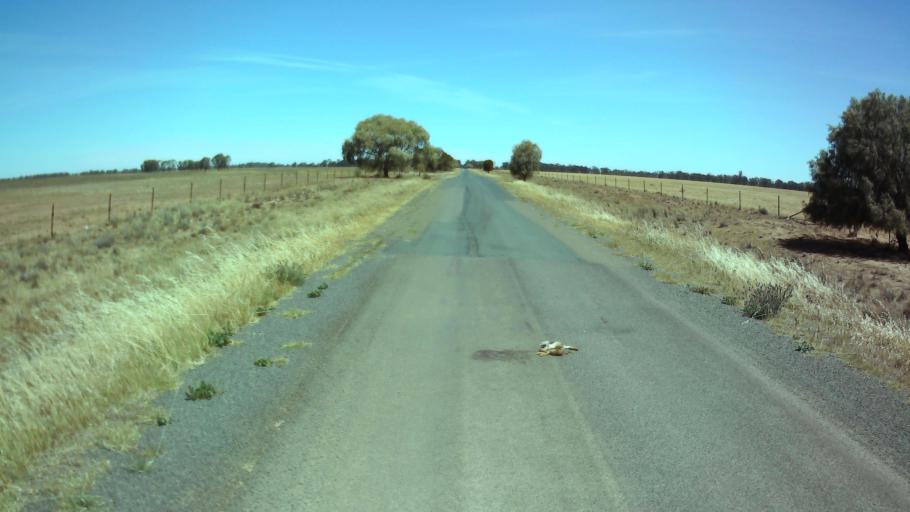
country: AU
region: New South Wales
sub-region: Weddin
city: Grenfell
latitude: -33.8530
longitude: 147.6952
